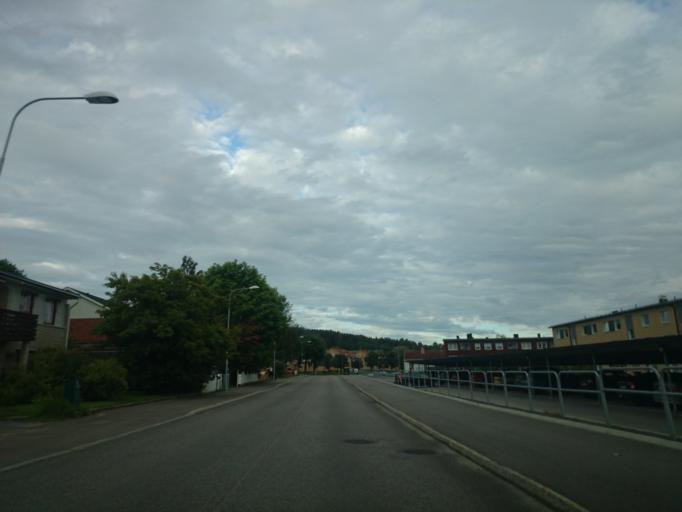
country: SE
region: Vaesternorrland
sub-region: Sundsvalls Kommun
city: Sundsvall
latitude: 62.4058
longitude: 17.2568
